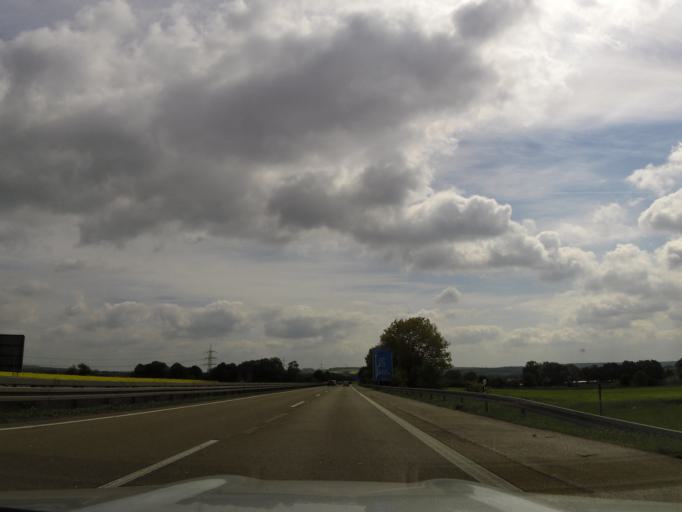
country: DE
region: Hesse
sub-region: Regierungsbezirk Giessen
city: Hoernsheim
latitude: 50.5265
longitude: 8.6217
